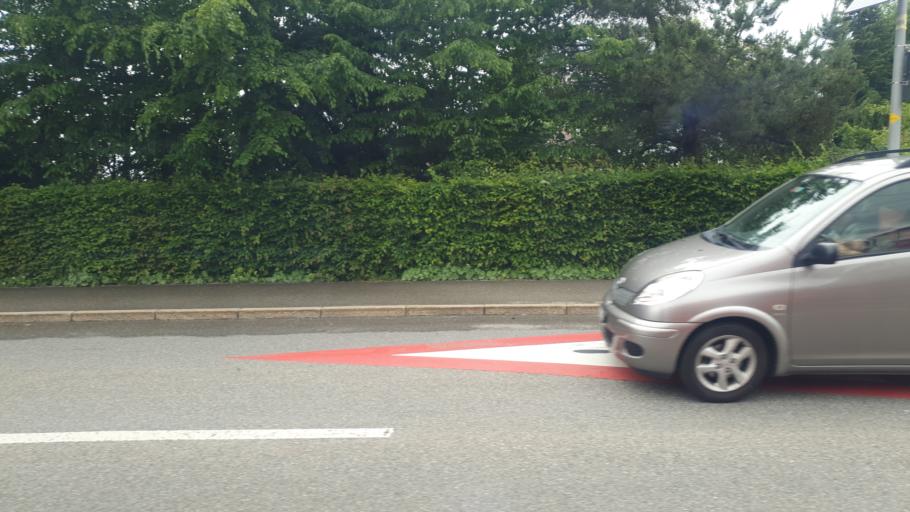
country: CH
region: Appenzell Ausserrhoden
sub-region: Bezirk Mittelland
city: Teufen
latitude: 47.3944
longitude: 9.3641
